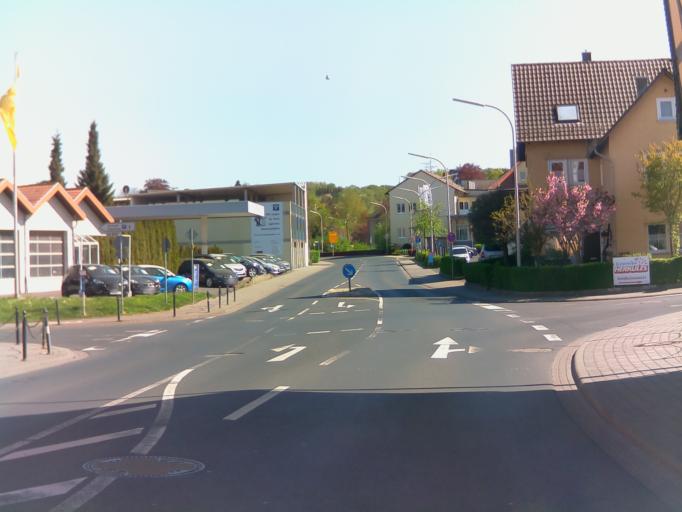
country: DE
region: Hesse
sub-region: Regierungsbezirk Giessen
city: Lauterbach
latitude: 50.6357
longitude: 9.3934
